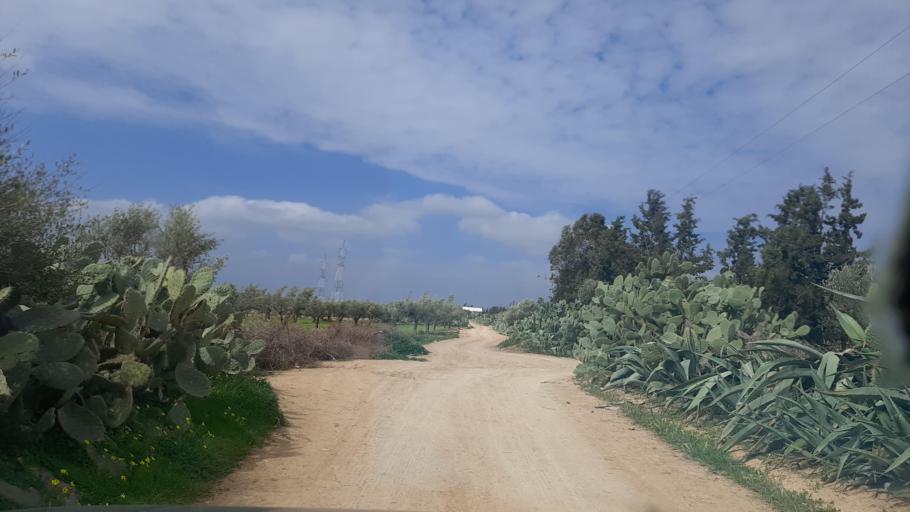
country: TN
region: Tunis
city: La Mohammedia
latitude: 36.6845
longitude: 10.0121
